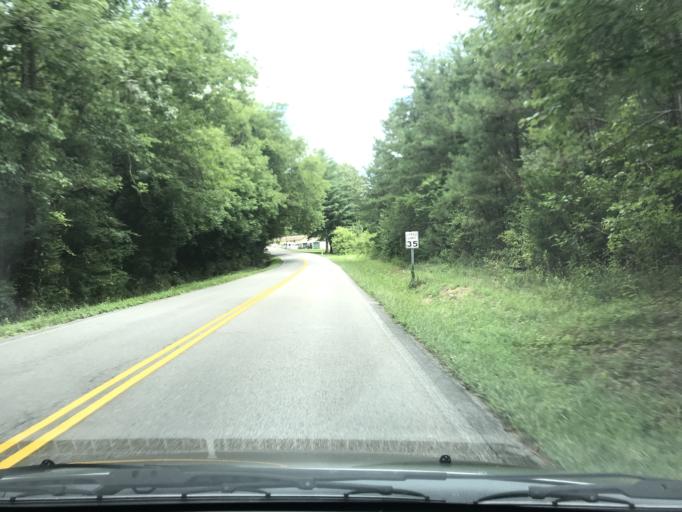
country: US
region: Tennessee
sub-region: Hamilton County
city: Lakesite
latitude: 35.1720
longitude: -85.0863
